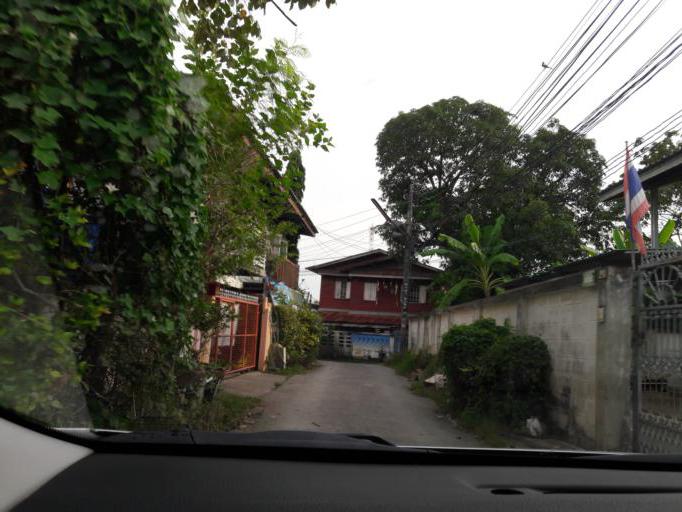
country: TH
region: Ang Thong
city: Ang Thong
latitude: 14.5885
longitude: 100.4559
